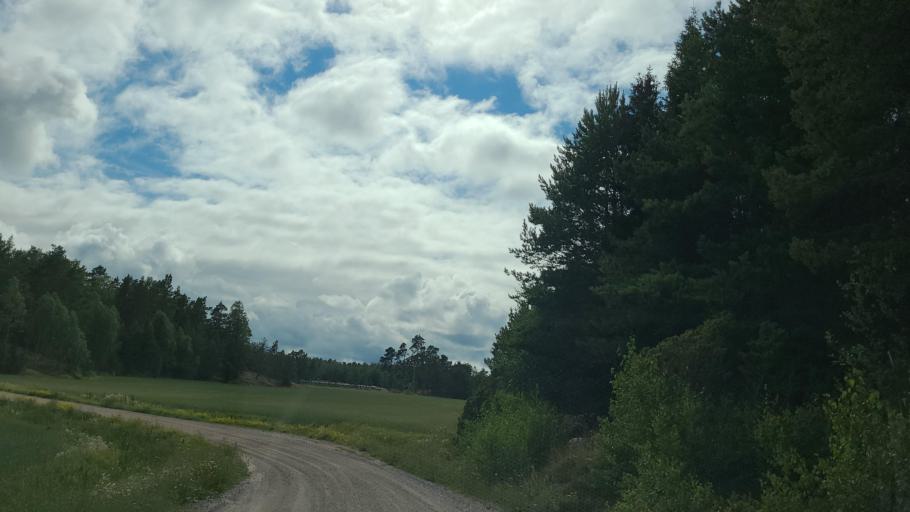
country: FI
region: Varsinais-Suomi
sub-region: Aboland-Turunmaa
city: Nagu
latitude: 60.1925
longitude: 21.7610
